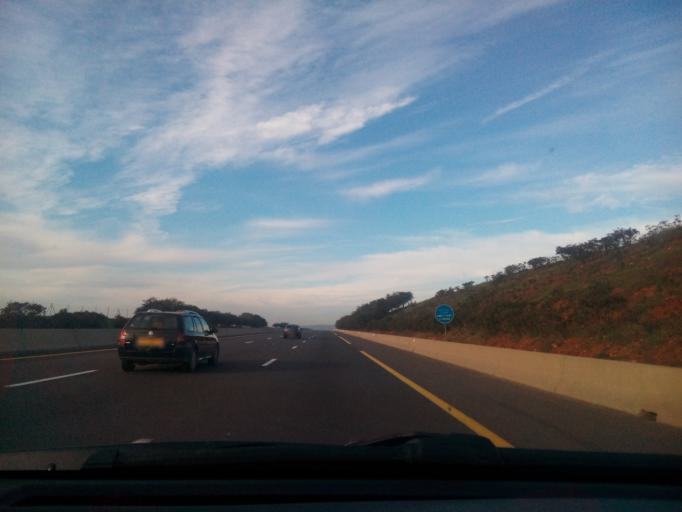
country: DZ
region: Relizane
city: Relizane
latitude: 35.7154
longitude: 0.2848
